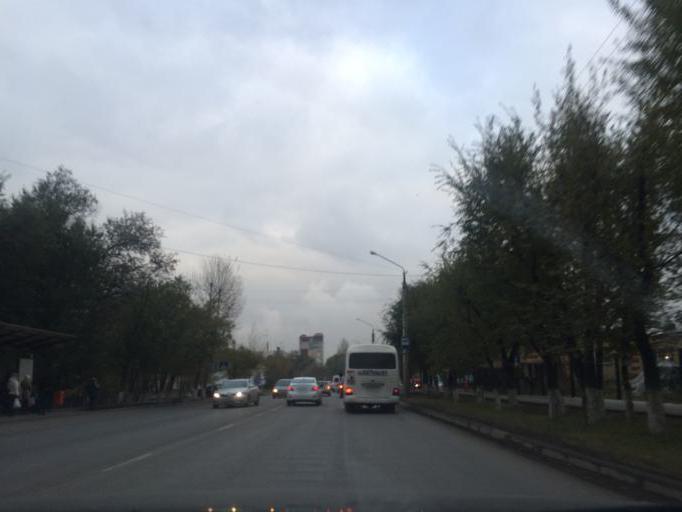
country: KZ
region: Astana Qalasy
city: Astana
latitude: 51.1940
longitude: 71.3997
